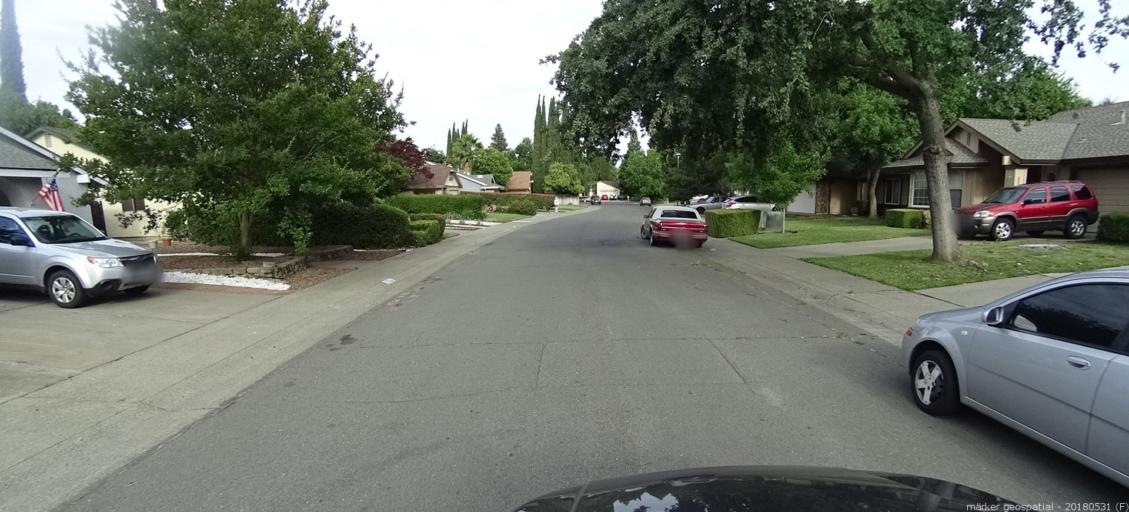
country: US
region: California
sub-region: Sacramento County
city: Sacramento
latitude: 38.6208
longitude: -121.4865
